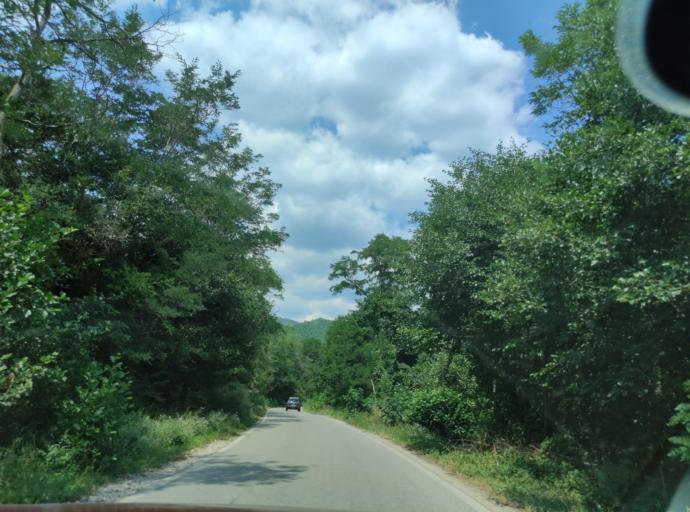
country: BG
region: Blagoevgrad
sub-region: Obshtina Belitsa
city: Belitsa
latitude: 41.9950
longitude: 23.5497
